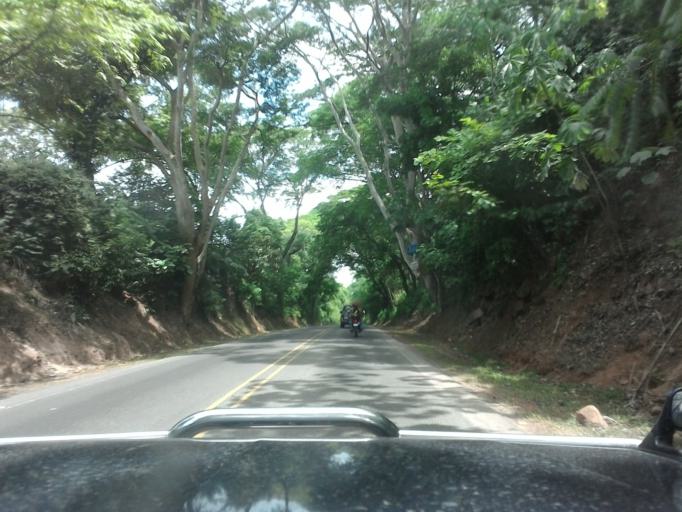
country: CR
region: Puntarenas
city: Miramar
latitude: 10.0673
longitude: -84.7665
